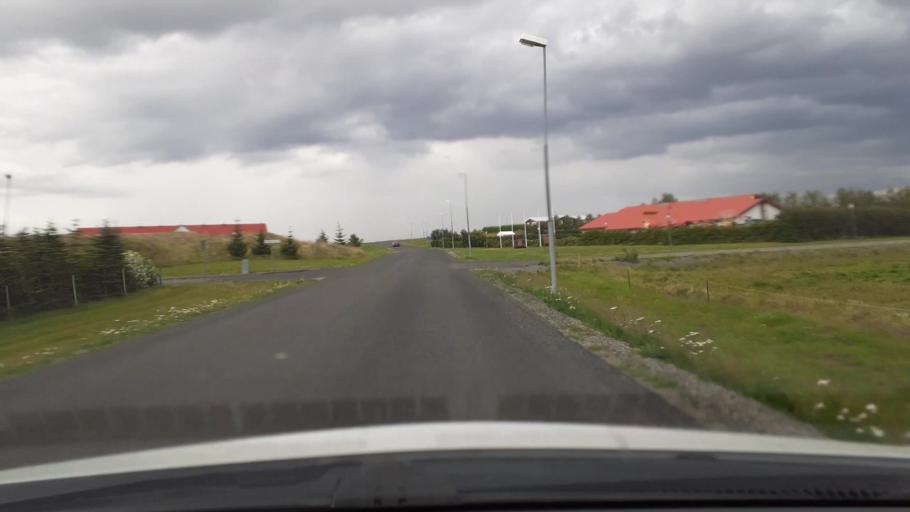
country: IS
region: West
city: Borgarnes
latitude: 64.5638
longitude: -21.7612
